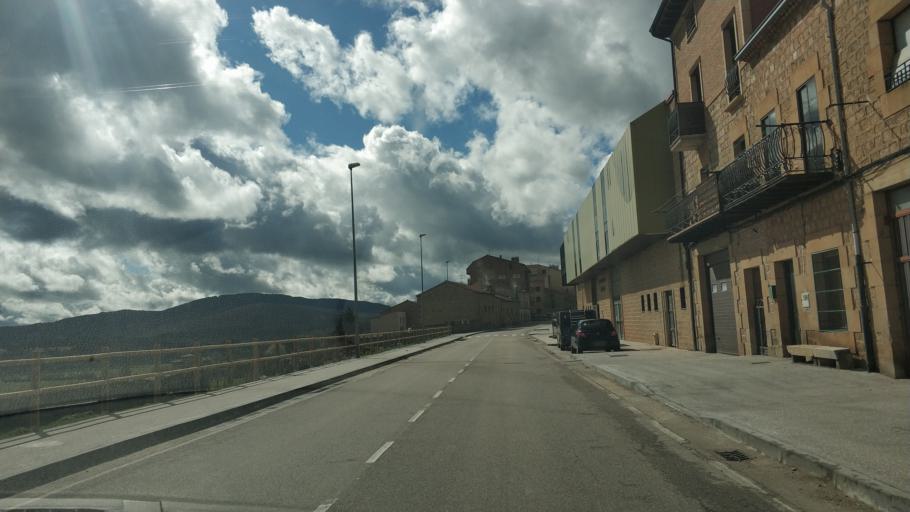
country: ES
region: Castille and Leon
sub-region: Provincia de Burgos
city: Quintanar de la Sierra
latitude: 41.9839
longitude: -3.0347
